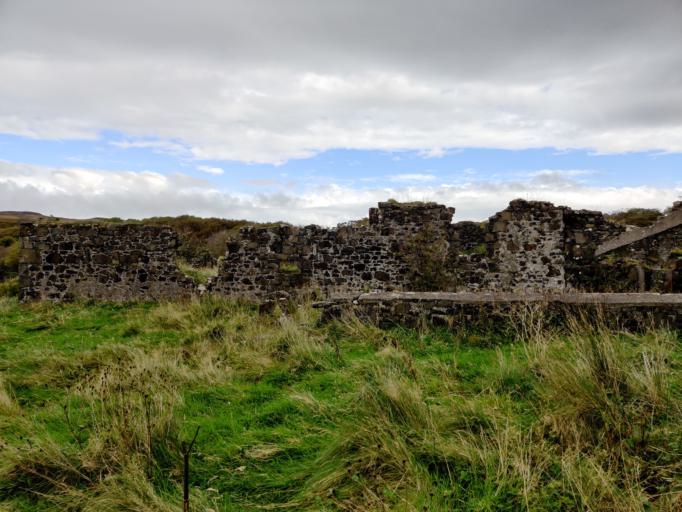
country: GB
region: Scotland
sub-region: Highland
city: Isle of Skye
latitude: 57.4520
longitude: -6.5945
